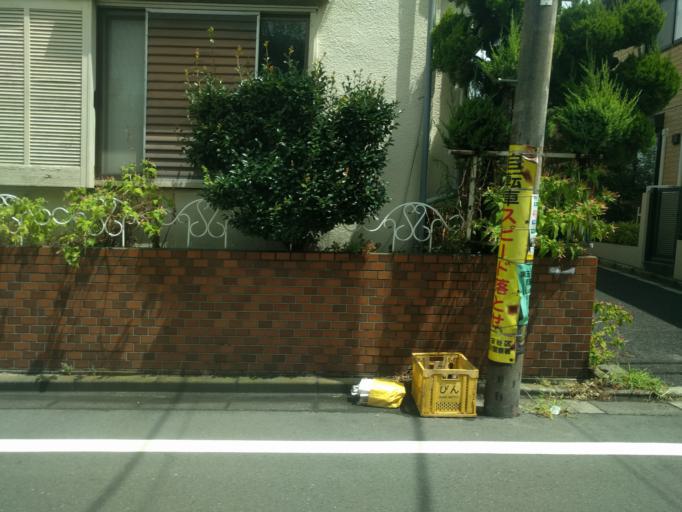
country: JP
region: Kanagawa
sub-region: Kawasaki-shi
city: Kawasaki
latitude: 35.5962
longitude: 139.6762
